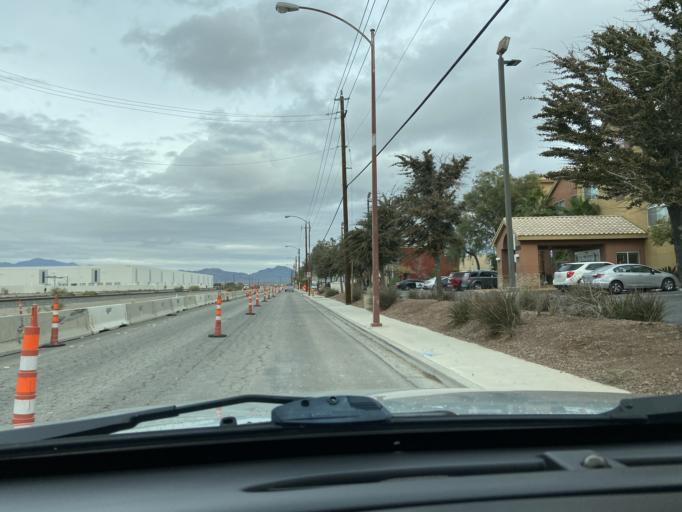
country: US
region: Nevada
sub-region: Clark County
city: Sunrise Manor
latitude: 36.2420
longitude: -115.1047
